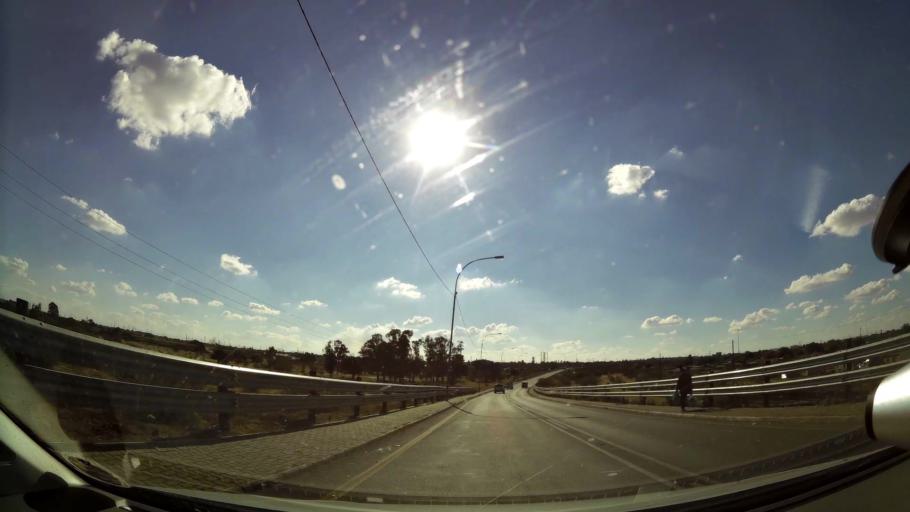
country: ZA
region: Northern Cape
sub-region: Frances Baard District Municipality
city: Kimberley
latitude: -28.7781
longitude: 24.7659
